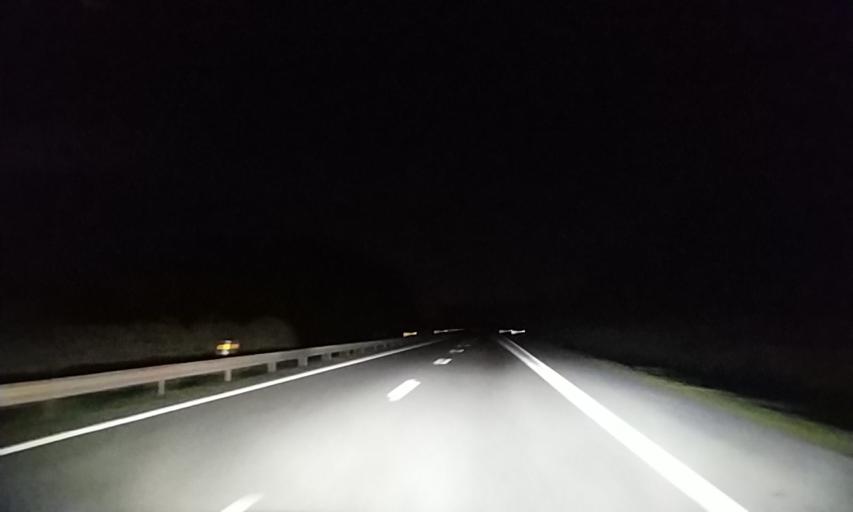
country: PT
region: Aveiro
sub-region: Estarreja
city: Salreu
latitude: 40.7222
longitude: -8.5222
